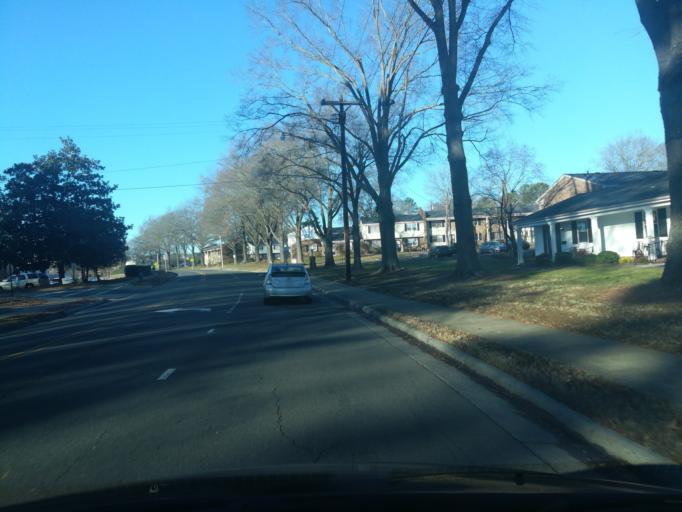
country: US
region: North Carolina
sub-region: Orange County
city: Chapel Hill
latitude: 35.9305
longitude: -79.0253
